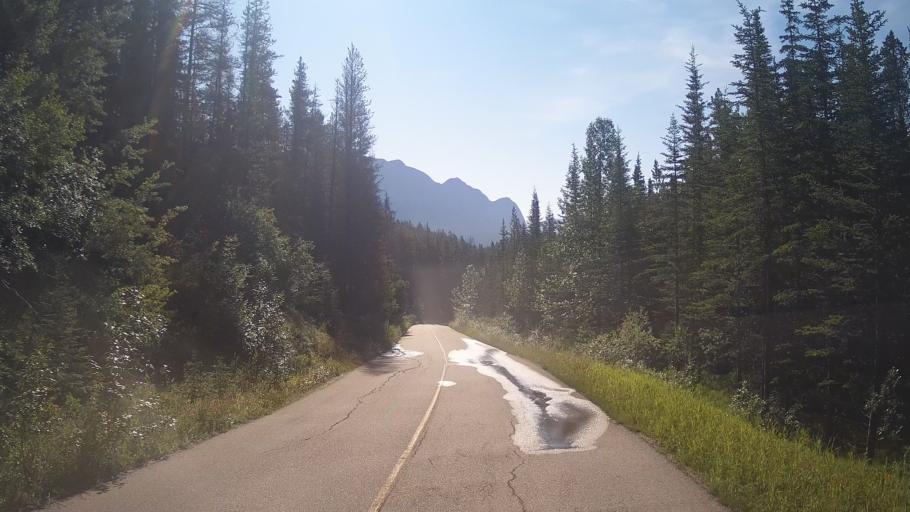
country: CA
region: Alberta
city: Jasper Park Lodge
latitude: 53.1784
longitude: -117.8633
